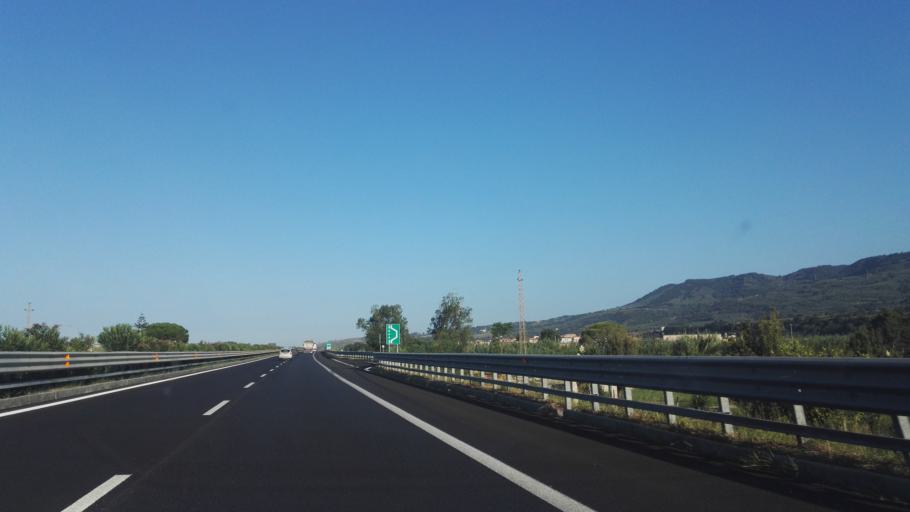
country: IT
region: Calabria
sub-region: Provincia di Catanzaro
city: Santa Eufemia Lamezia
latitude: 38.9326
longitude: 16.2250
